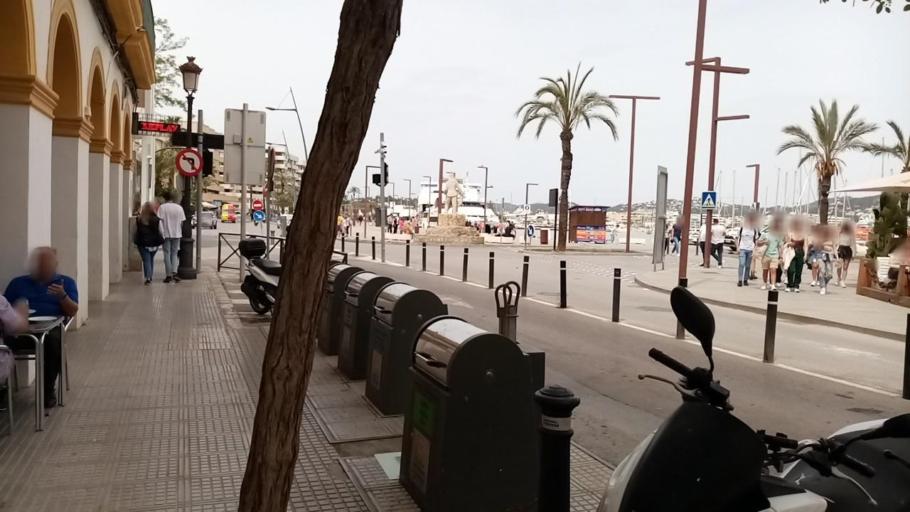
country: ES
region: Balearic Islands
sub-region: Illes Balears
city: Ibiza
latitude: 38.9102
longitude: 1.4348
